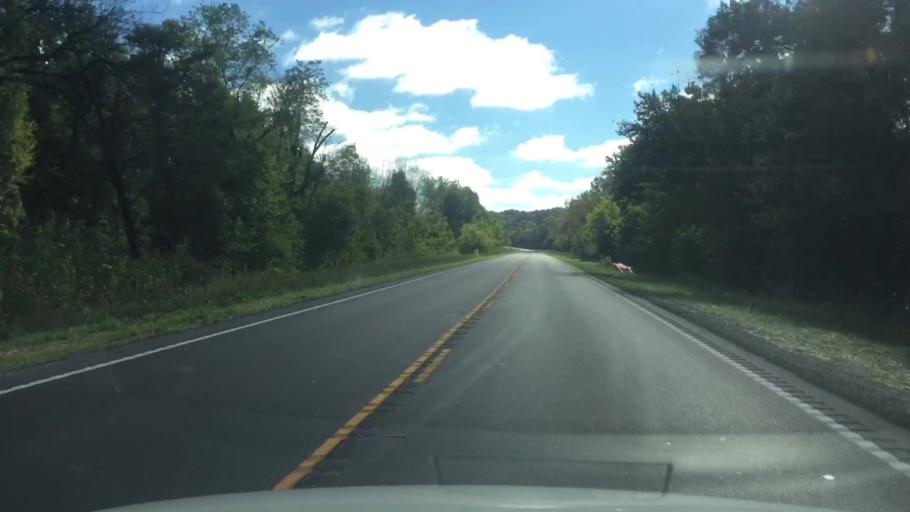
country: US
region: Missouri
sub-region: Howard County
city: New Franklin
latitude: 38.9870
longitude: -92.5543
